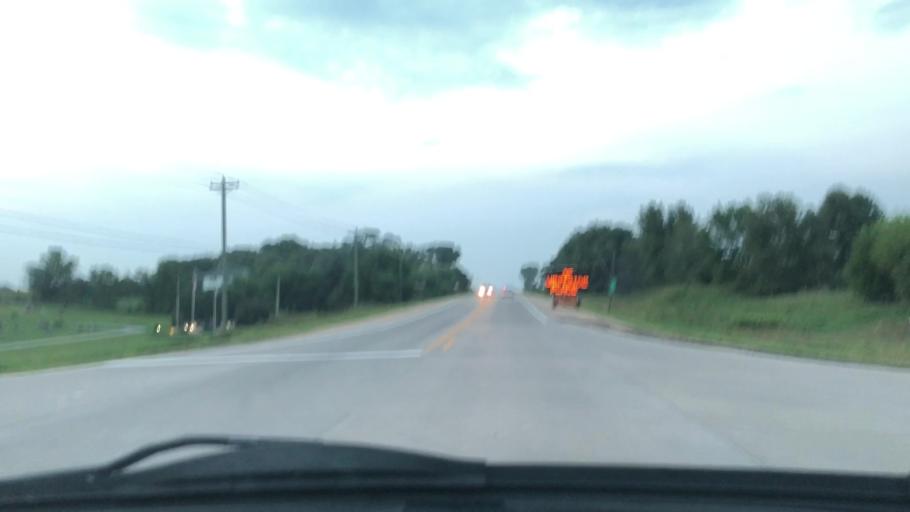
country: US
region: Iowa
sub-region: Linn County
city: Ely
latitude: 41.8479
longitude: -91.6754
